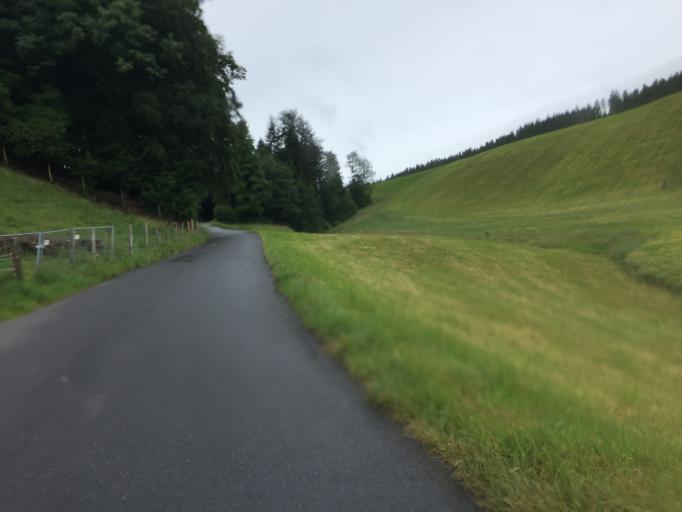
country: CH
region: Bern
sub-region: Bern-Mittelland District
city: Konolfingen
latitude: 46.8882
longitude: 7.6211
